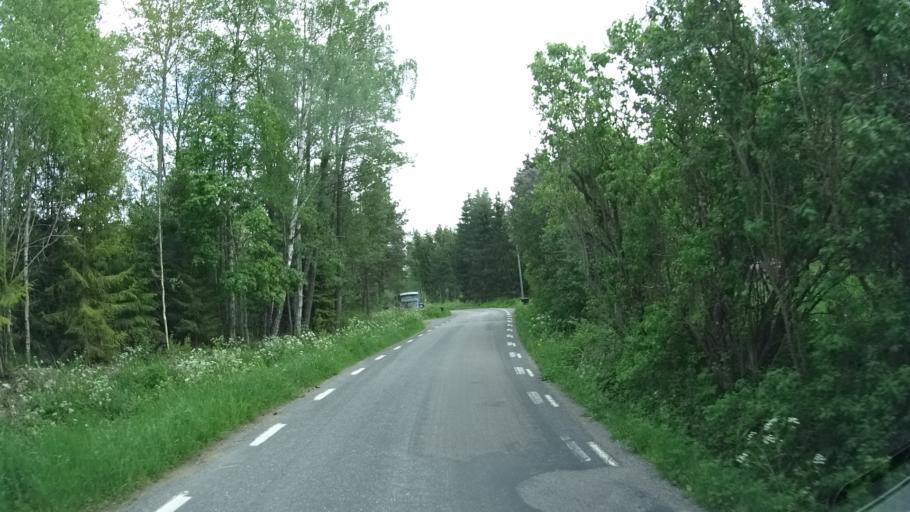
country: SE
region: OEstergoetland
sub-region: Finspangs Kommun
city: Finspang
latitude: 58.5971
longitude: 15.7671
